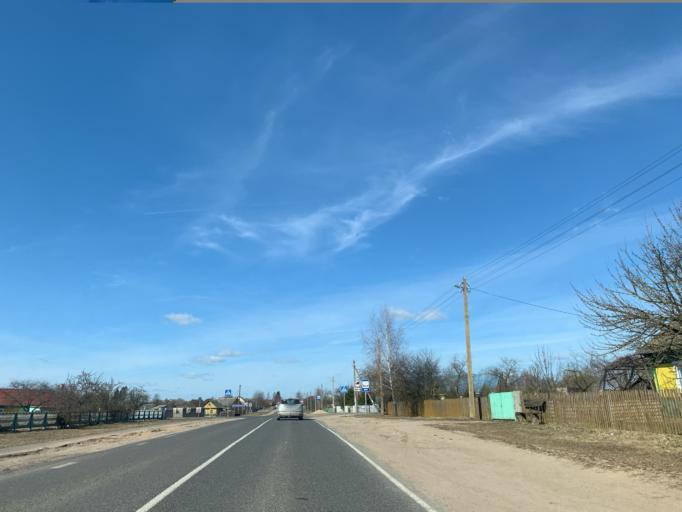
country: BY
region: Minsk
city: Haradzyeya
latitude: 53.3110
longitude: 26.5534
